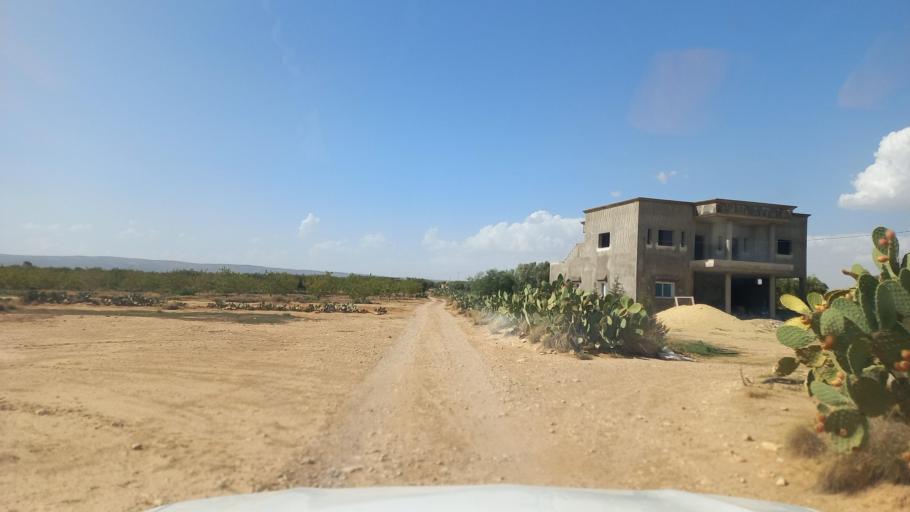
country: TN
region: Al Qasrayn
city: Kasserine
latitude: 35.2695
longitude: 9.0245
